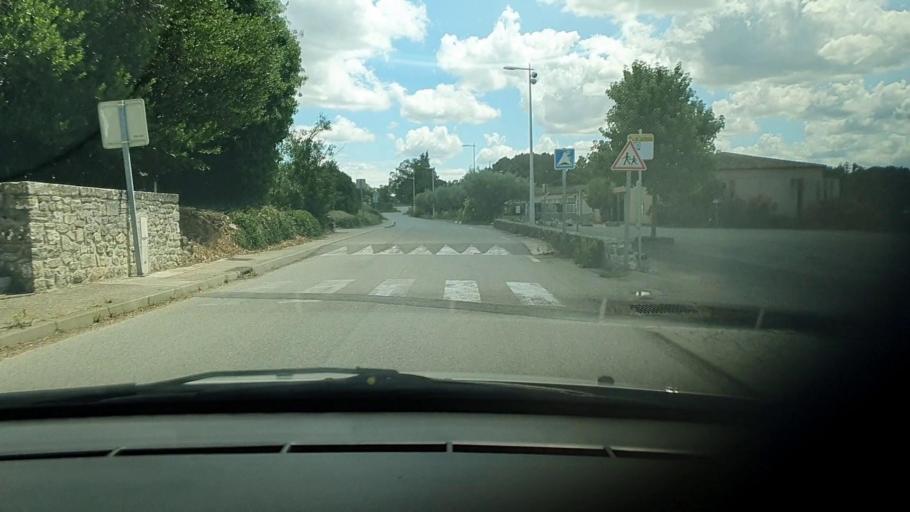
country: FR
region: Languedoc-Roussillon
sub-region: Departement du Gard
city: Moussac
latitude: 44.0505
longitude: 4.2283
